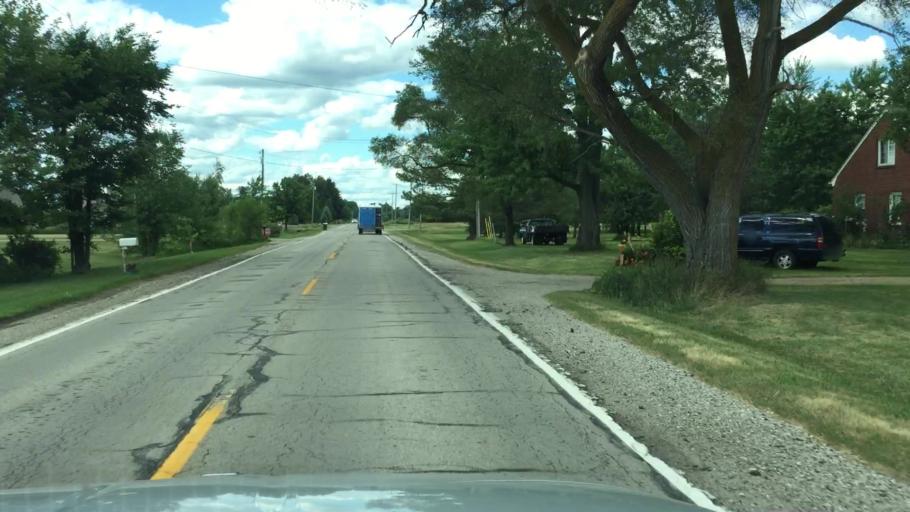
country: US
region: Michigan
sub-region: Saint Clair County
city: Capac
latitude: 42.9283
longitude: -82.9457
